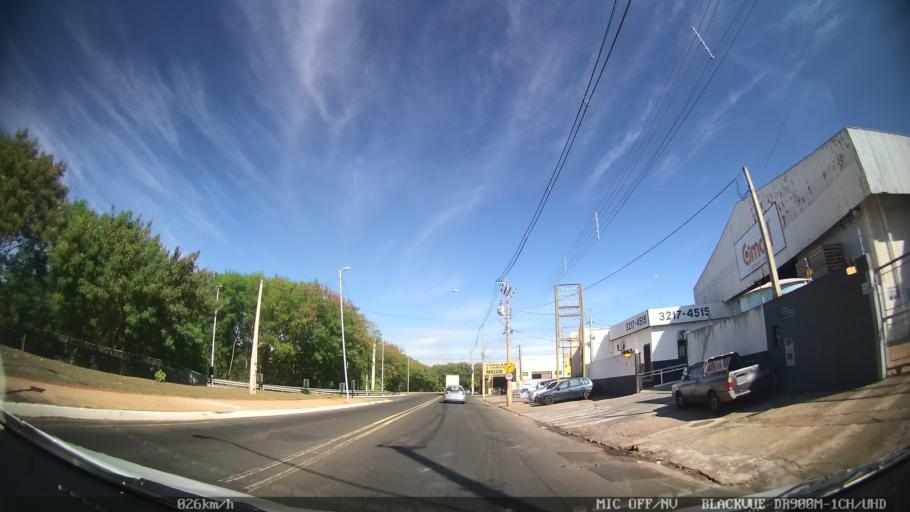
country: BR
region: Sao Paulo
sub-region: Sao Jose Do Rio Preto
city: Sao Jose do Rio Preto
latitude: -20.8023
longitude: -49.4087
